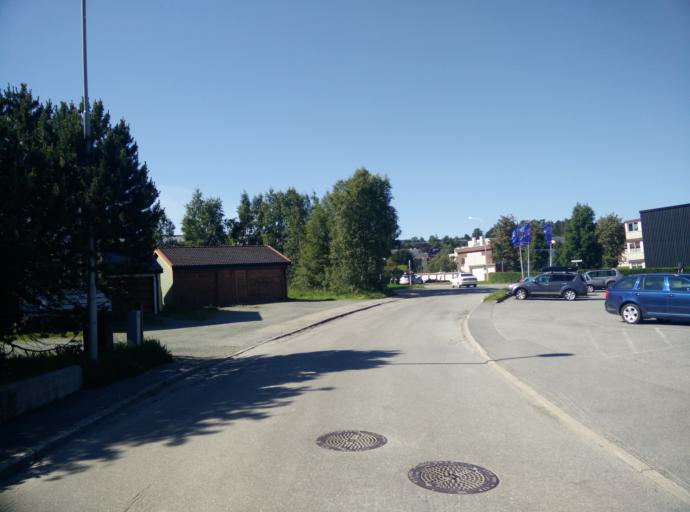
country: NO
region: Sor-Trondelag
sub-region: Trondheim
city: Trondheim
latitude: 63.4087
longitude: 10.3615
